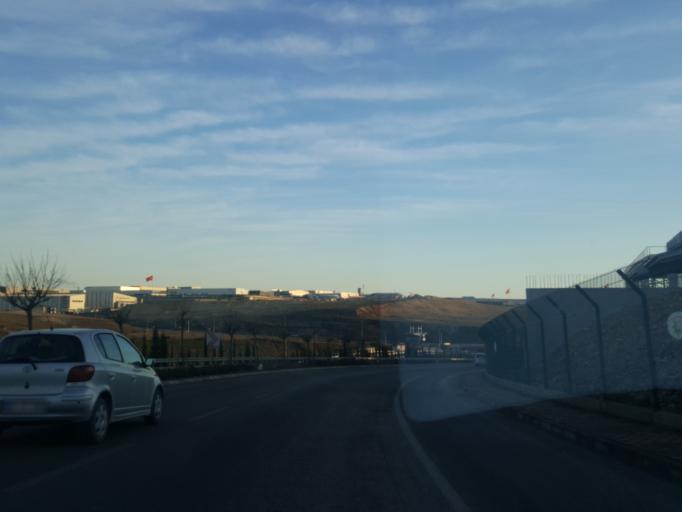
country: TR
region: Kocaeli
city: Tavsanli
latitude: 40.8242
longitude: 29.5587
